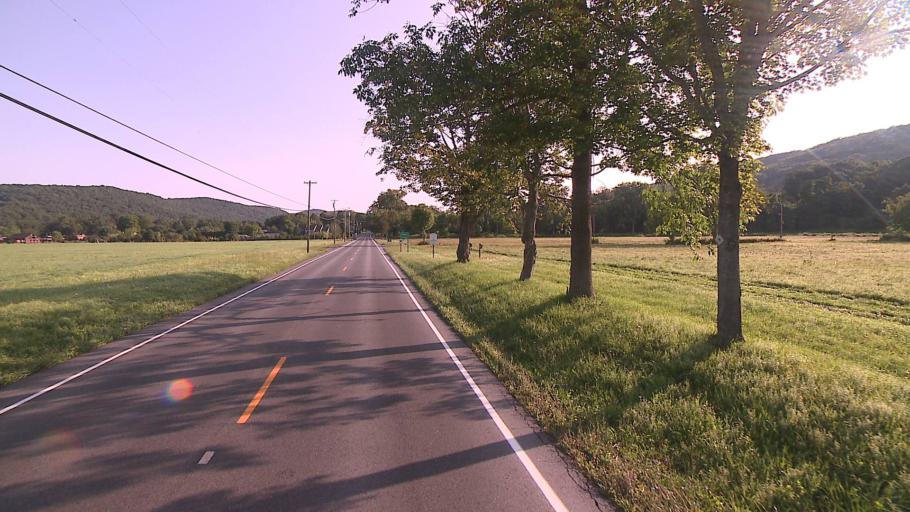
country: US
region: Connecticut
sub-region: Litchfield County
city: Kent
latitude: 41.7195
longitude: -73.4805
